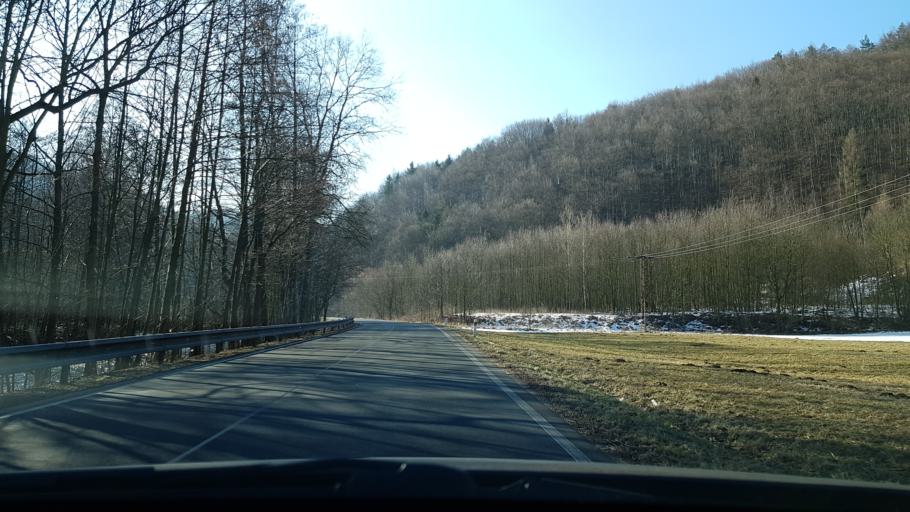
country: CZ
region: Olomoucky
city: Dolni Bohdikov
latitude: 50.0474
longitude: 16.9150
